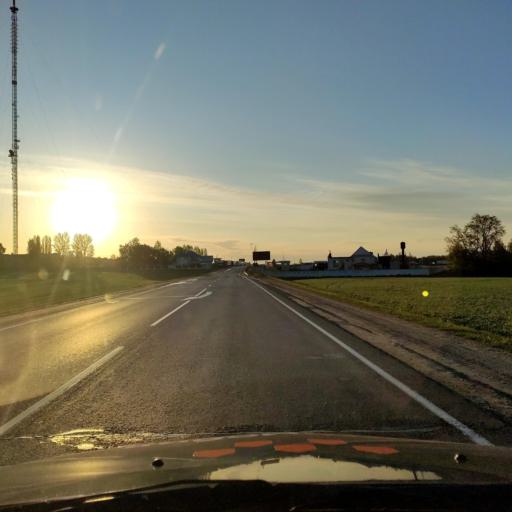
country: RU
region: Orjol
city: Livny
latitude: 52.4495
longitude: 37.4956
